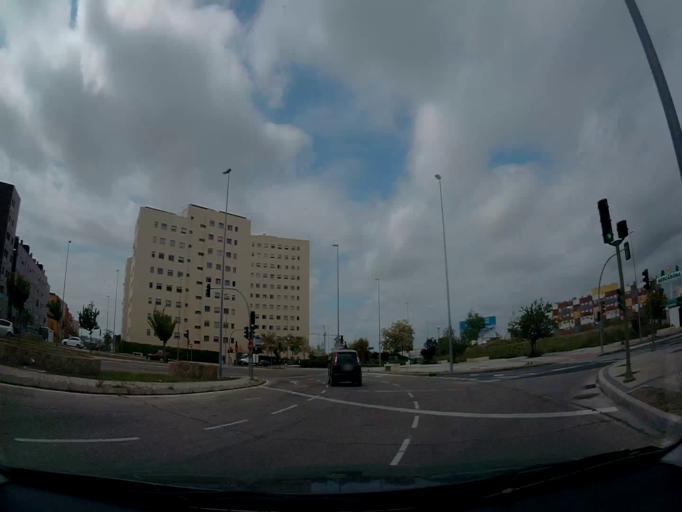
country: ES
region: Madrid
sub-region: Provincia de Madrid
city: Alcorcon
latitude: 40.3295
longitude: -3.8351
